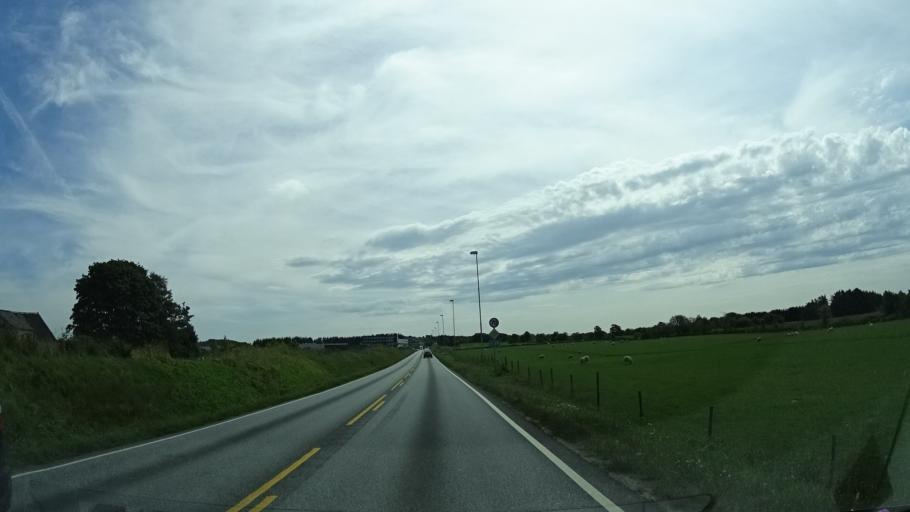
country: NO
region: Rogaland
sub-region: Randaberg
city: Randaberg
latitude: 58.9995
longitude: 5.6460
